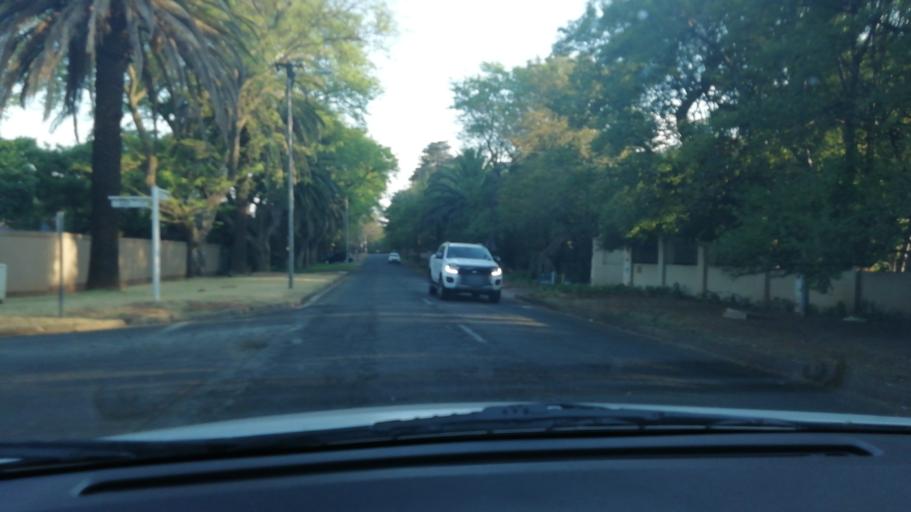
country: ZA
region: Gauteng
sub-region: Ekurhuleni Metropolitan Municipality
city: Benoni
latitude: -26.1935
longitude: 28.2886
